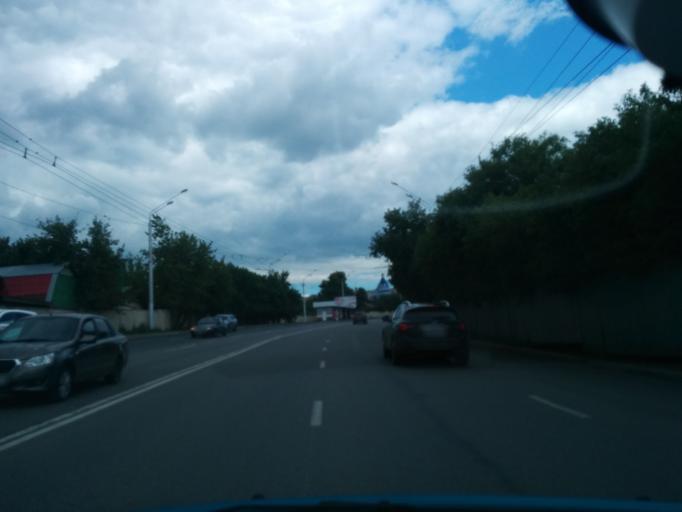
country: RU
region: Bashkortostan
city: Ufa
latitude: 54.7224
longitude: 55.9758
